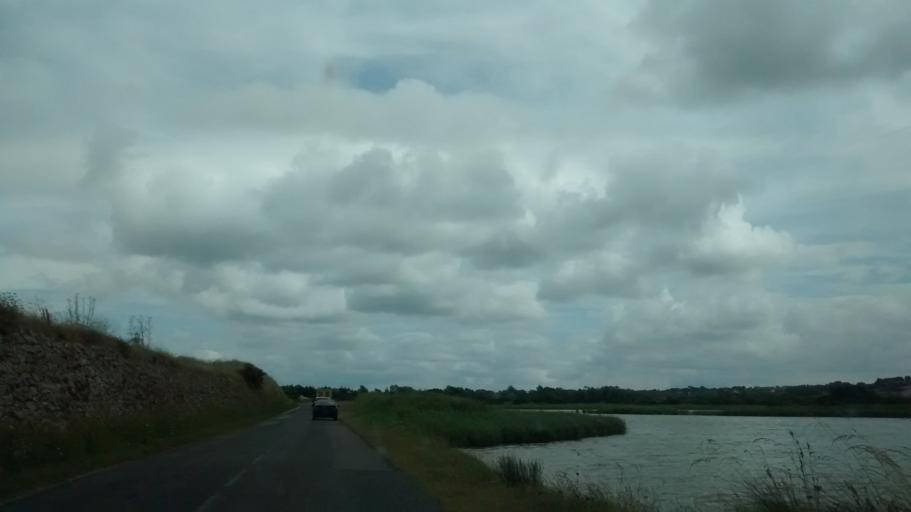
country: FR
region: Brittany
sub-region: Departement du Finistere
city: Guisseny
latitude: 48.6356
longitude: -4.4356
